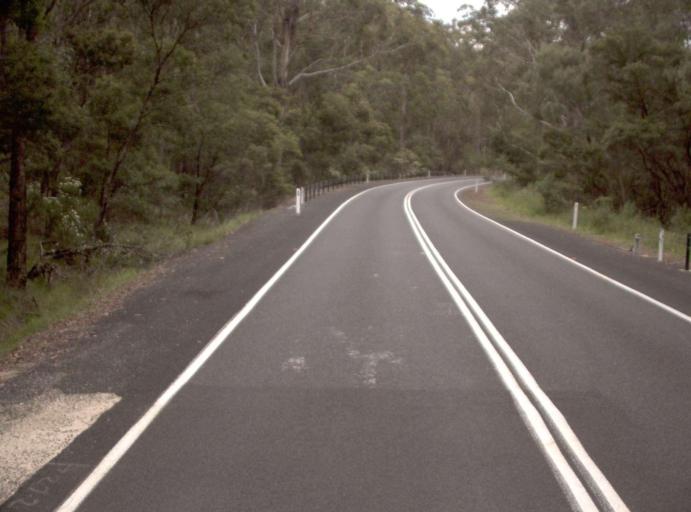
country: AU
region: New South Wales
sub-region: Bombala
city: Bombala
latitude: -37.3550
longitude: 149.2026
